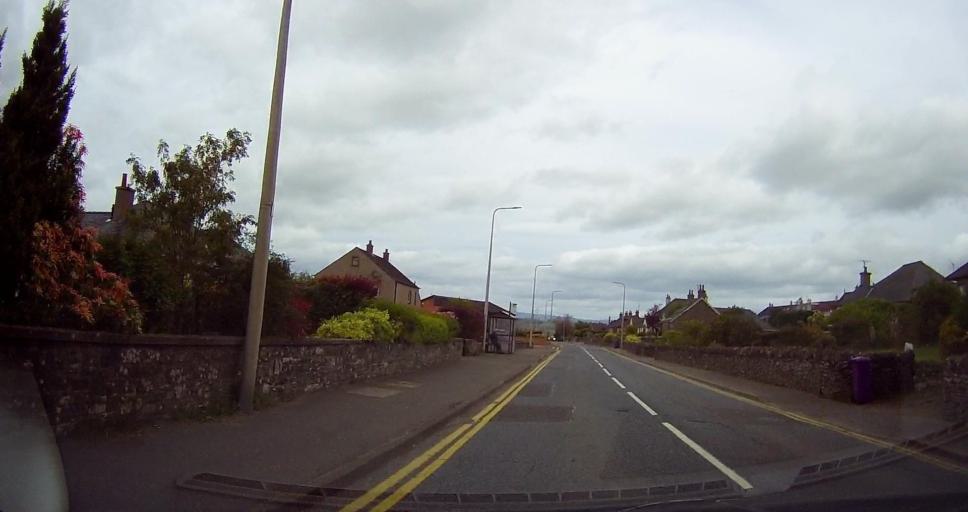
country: GB
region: Scotland
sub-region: Angus
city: Forfar
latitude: 56.6318
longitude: -2.8963
